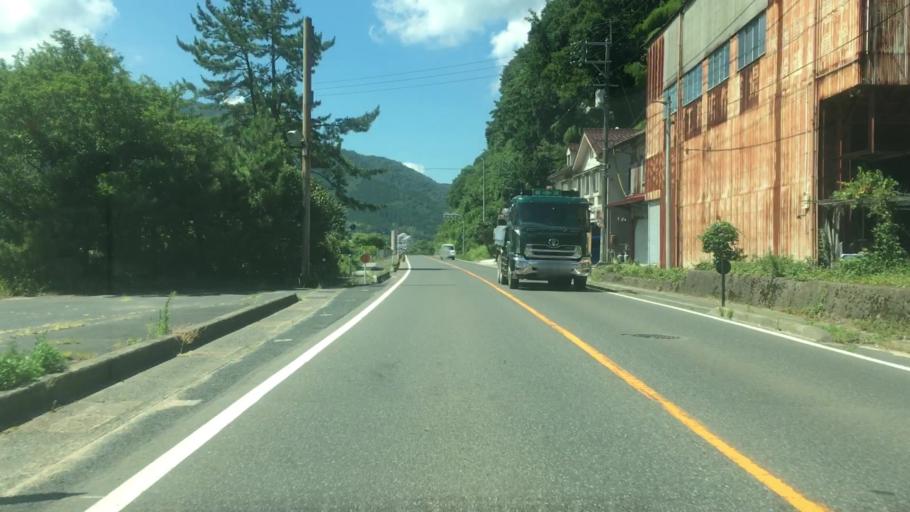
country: JP
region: Tottori
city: Tottori
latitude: 35.2555
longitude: 134.2292
